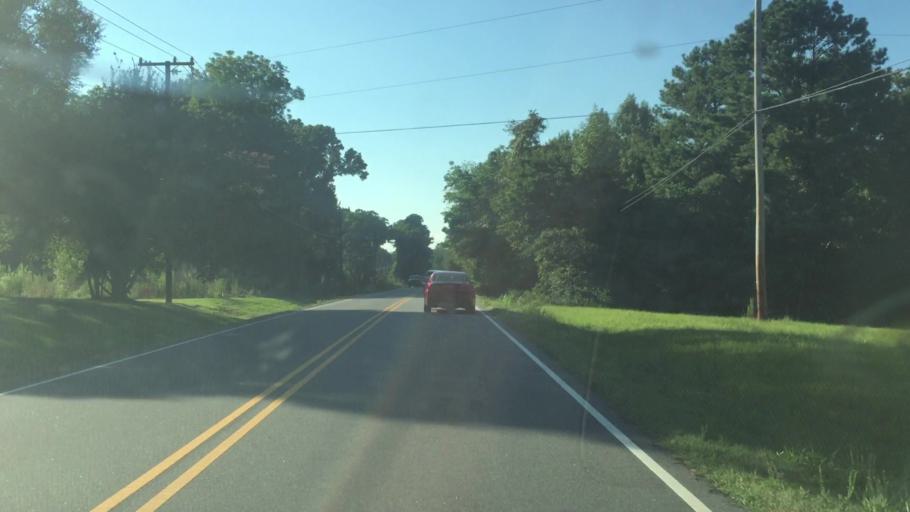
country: US
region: North Carolina
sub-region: Rowan County
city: Enochville
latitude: 35.4712
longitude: -80.7445
